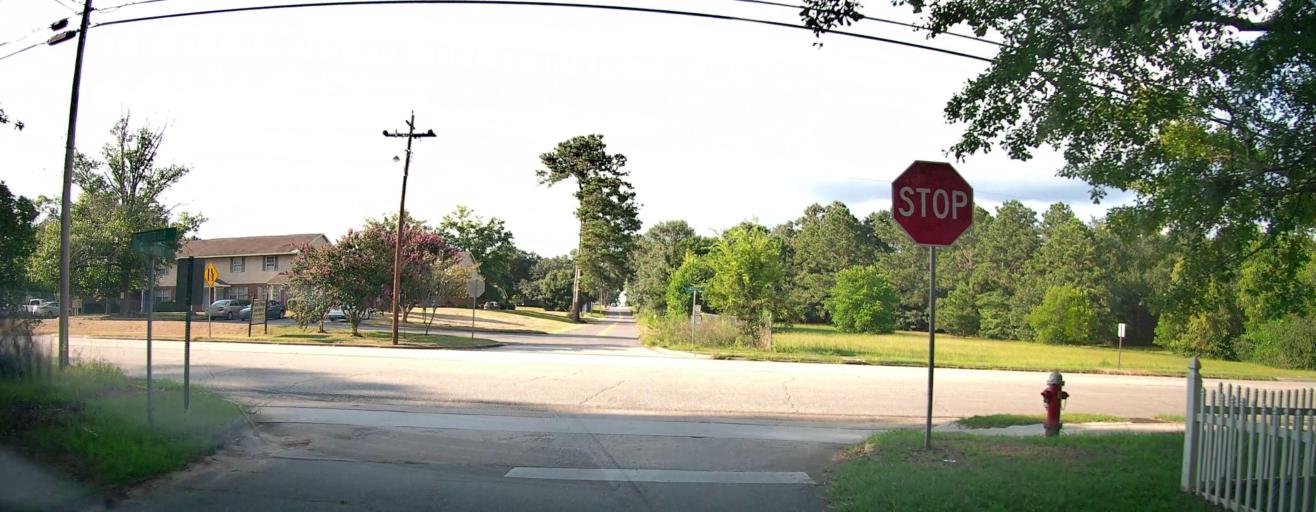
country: US
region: Georgia
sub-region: Crawford County
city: Roberta
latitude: 32.7212
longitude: -84.0162
